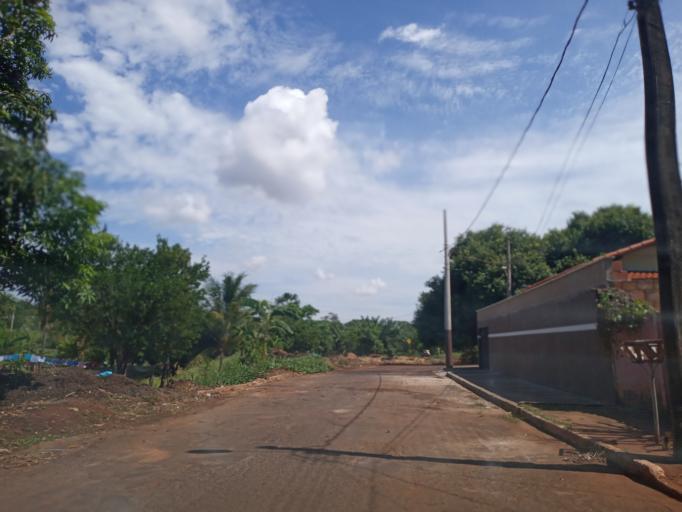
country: BR
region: Minas Gerais
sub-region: Ituiutaba
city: Ituiutaba
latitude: -18.9920
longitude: -49.4744
